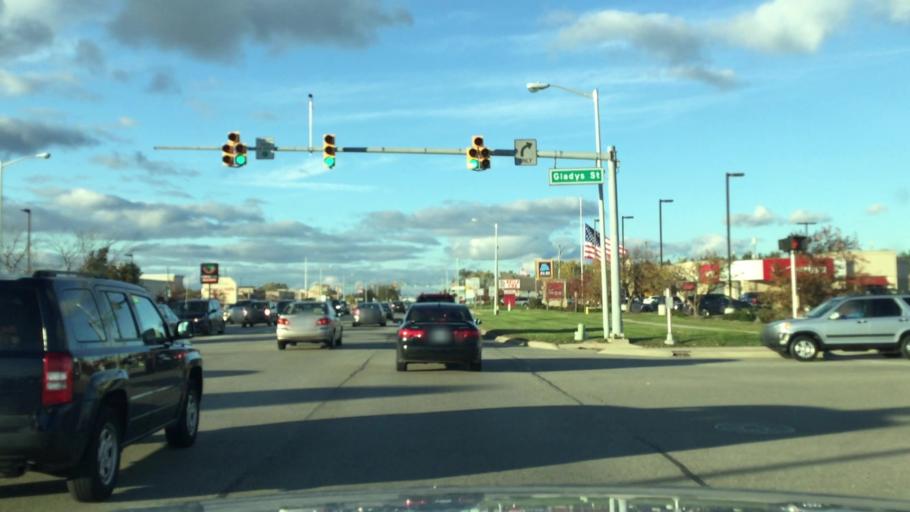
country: US
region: Michigan
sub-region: Kalamazoo County
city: Portage
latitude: 42.2246
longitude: -85.5894
